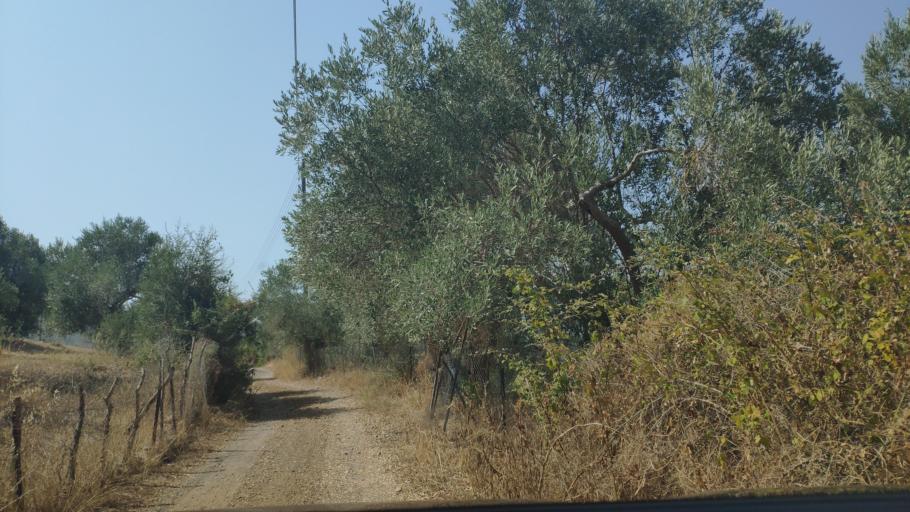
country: GR
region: West Greece
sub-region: Nomos Aitolias kai Akarnanias
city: Fitiai
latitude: 38.7244
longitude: 21.1909
